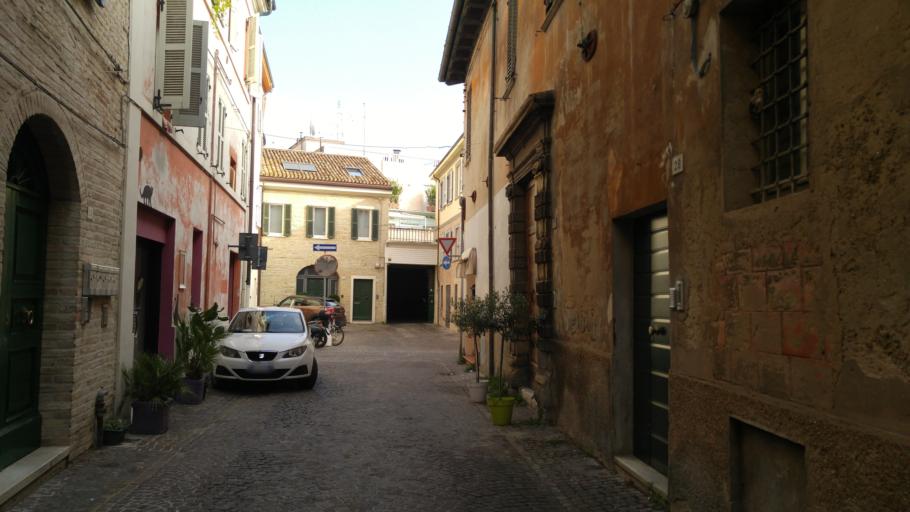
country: IT
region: The Marches
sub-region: Provincia di Pesaro e Urbino
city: Pesaro
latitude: 43.9085
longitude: 12.9116
